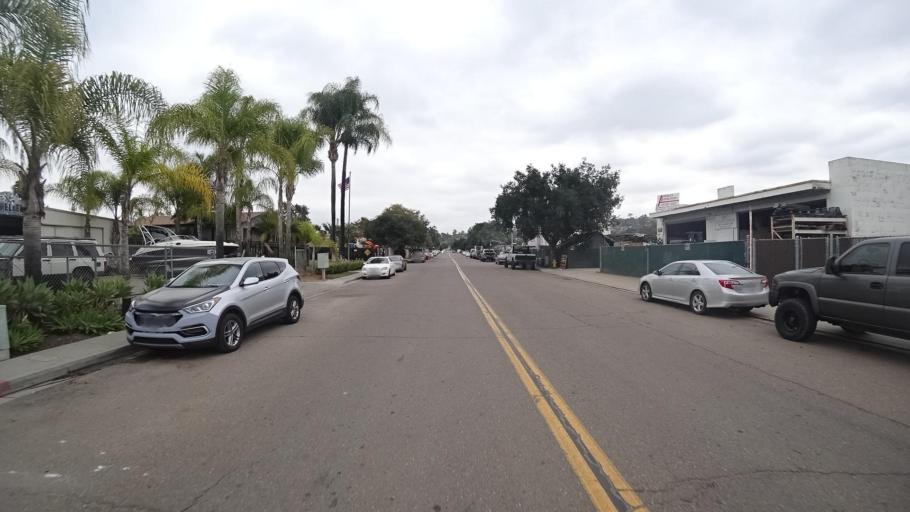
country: US
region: California
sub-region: San Diego County
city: Spring Valley
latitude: 32.7420
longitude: -117.0041
